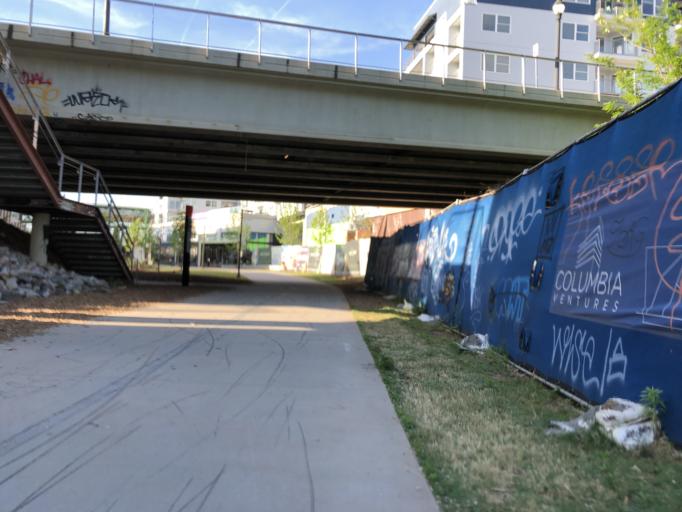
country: US
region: Georgia
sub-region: Fulton County
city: Atlanta
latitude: 33.7546
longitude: -84.3655
